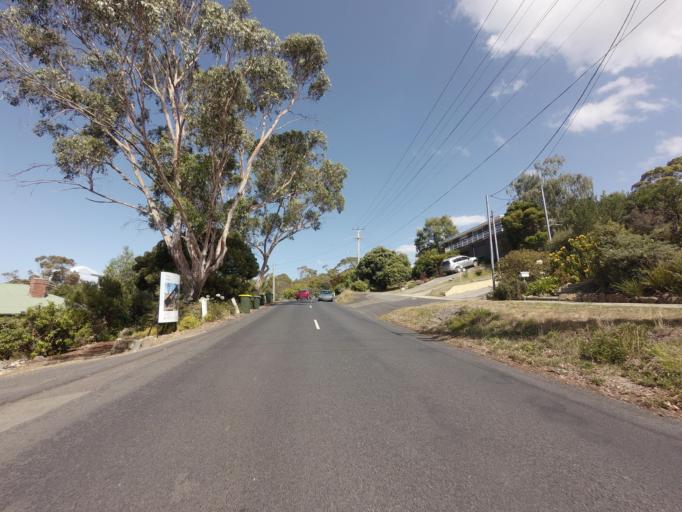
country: AU
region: Tasmania
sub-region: Hobart
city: Dynnyrne
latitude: -42.9181
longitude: 147.3238
